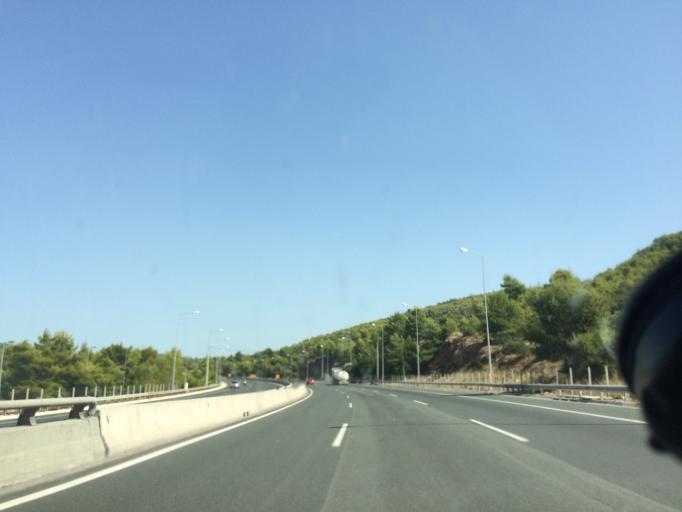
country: GR
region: Attica
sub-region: Nomarchia Anatolikis Attikis
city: Afidnes
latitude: 38.2289
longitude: 23.8177
